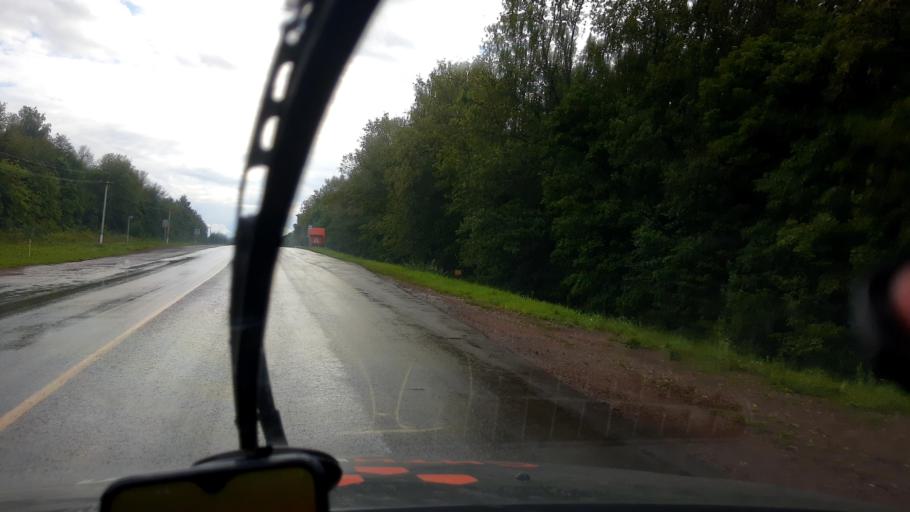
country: RU
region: Bashkortostan
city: Tolbazy
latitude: 53.9219
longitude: 56.3501
